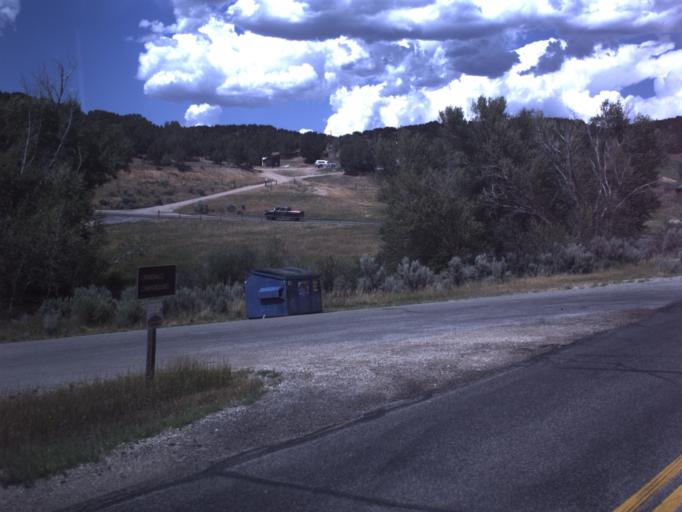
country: US
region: Utah
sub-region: Summit County
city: Oakley
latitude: 40.7653
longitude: -111.3813
